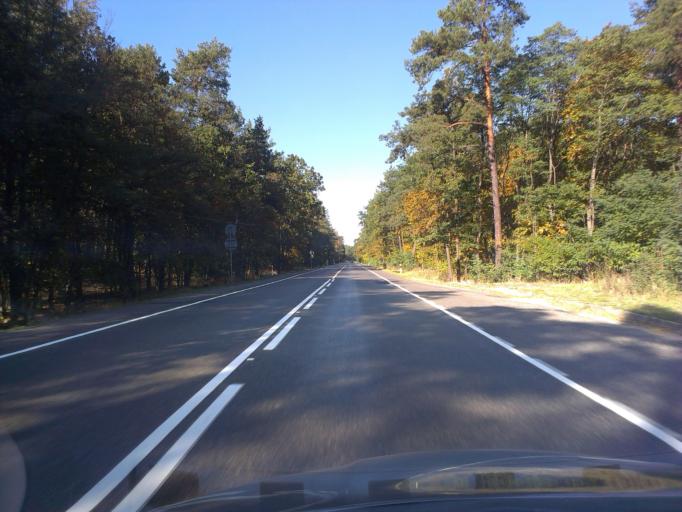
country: PL
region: Greater Poland Voivodeship
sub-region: Powiat chodzieski
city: Budzyn
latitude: 52.8393
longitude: 16.9722
